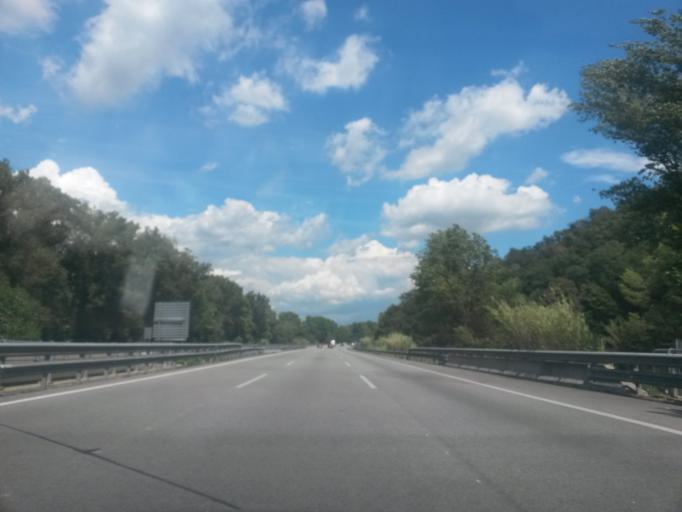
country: ES
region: Catalonia
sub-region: Provincia de Barcelona
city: Sant Celoni
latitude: 41.6873
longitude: 2.5015
